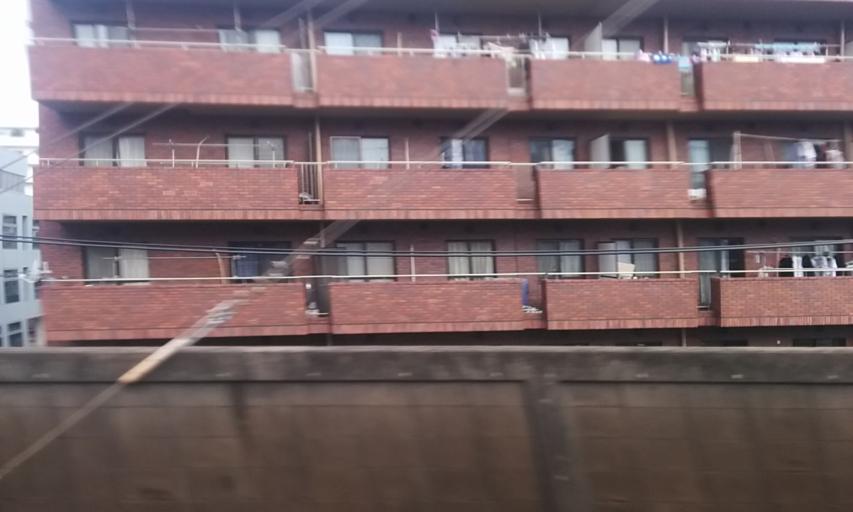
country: JP
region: Kanagawa
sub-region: Kawasaki-shi
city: Kawasaki
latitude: 35.5102
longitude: 139.6812
